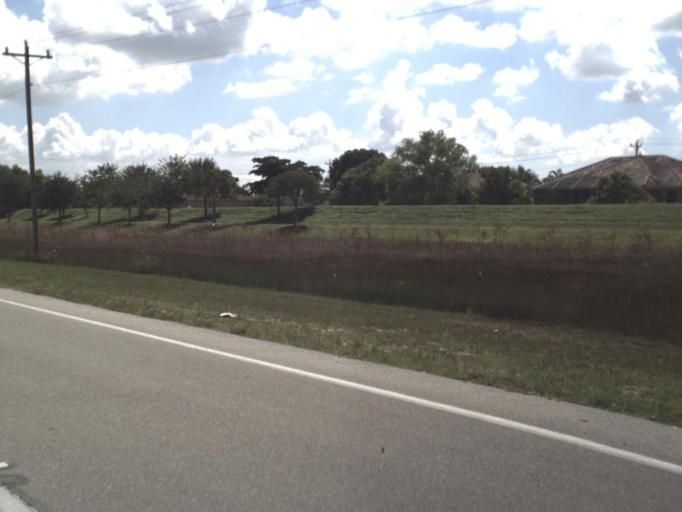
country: US
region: Florida
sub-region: Lee County
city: Cape Coral
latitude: 26.6070
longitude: -82.0182
